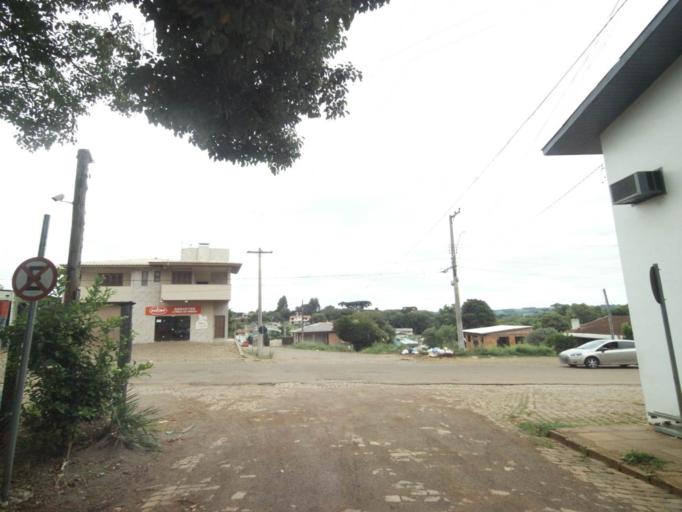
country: BR
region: Rio Grande do Sul
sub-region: Lagoa Vermelha
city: Lagoa Vermelha
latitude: -28.2125
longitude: -51.5274
